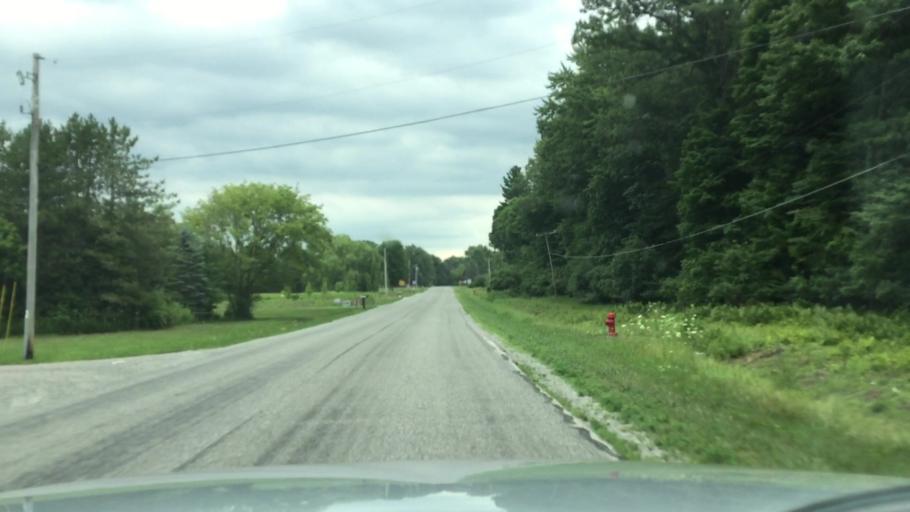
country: US
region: Michigan
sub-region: Saginaw County
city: Birch Run
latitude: 43.3217
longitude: -83.8143
